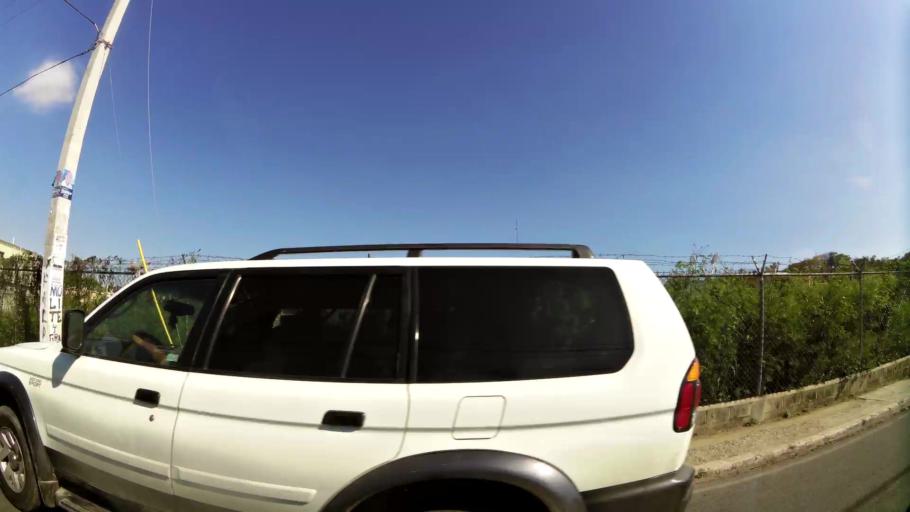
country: DO
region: San Cristobal
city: El Carril
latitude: 18.4649
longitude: -69.9983
